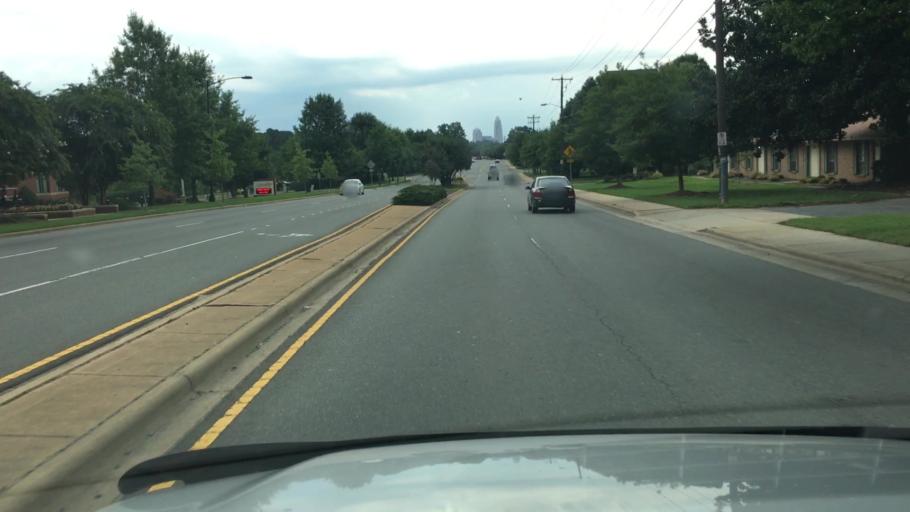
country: US
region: North Carolina
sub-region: Mecklenburg County
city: Charlotte
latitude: 35.2804
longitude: -80.8564
